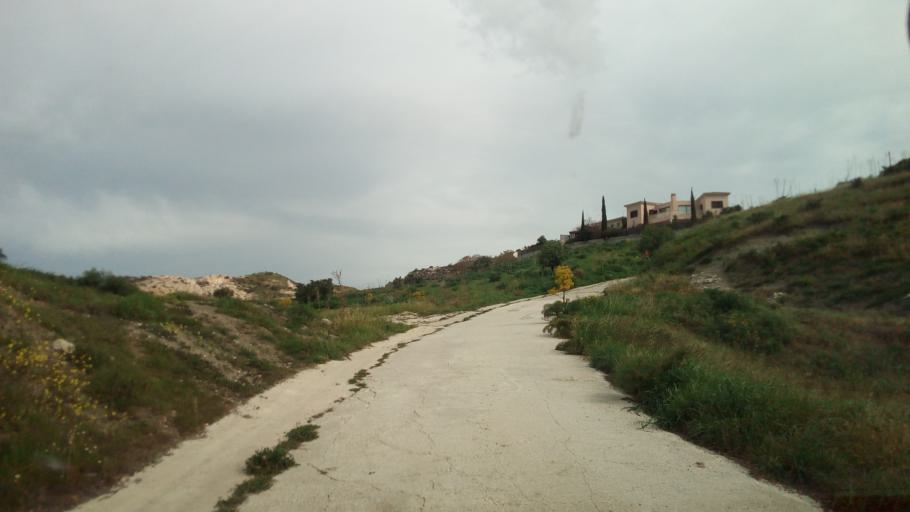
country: CY
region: Pafos
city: Mesogi
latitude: 34.7961
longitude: 32.4735
